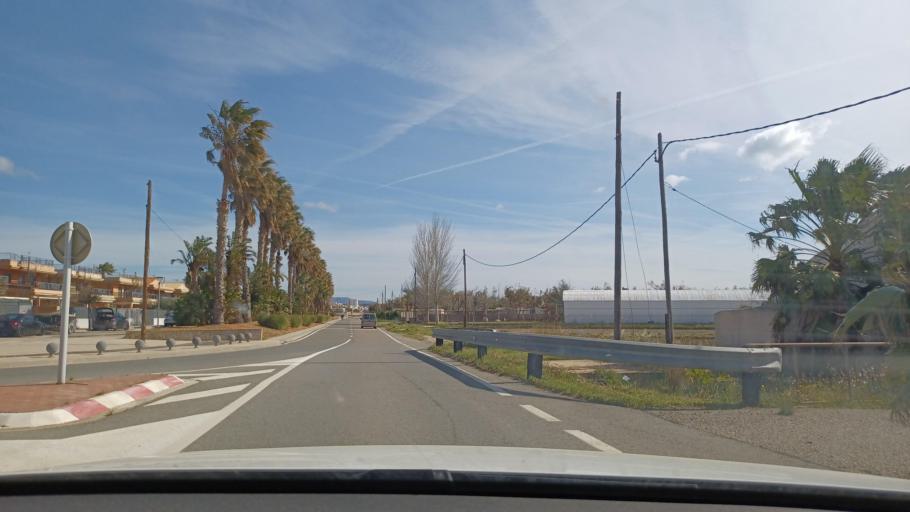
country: ES
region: Catalonia
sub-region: Provincia de Tarragona
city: L'Ampolla
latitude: 40.7981
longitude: 0.6966
